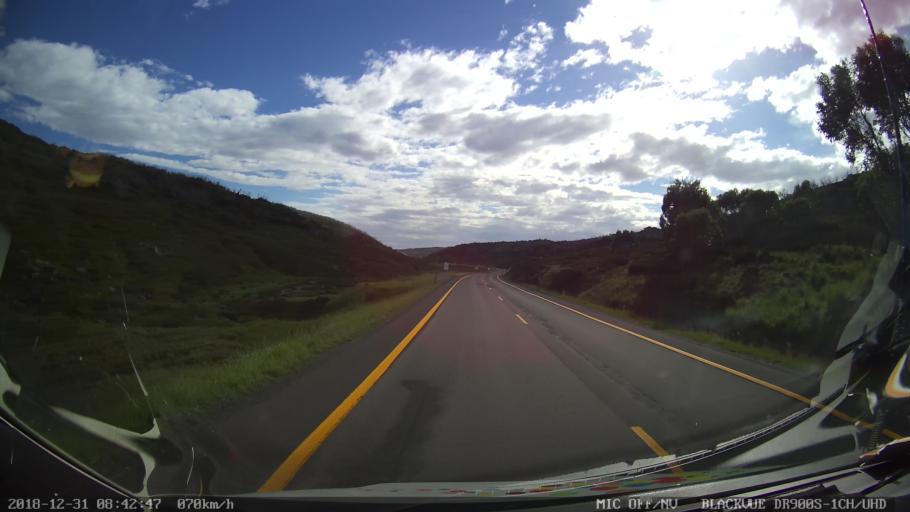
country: AU
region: New South Wales
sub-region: Snowy River
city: Jindabyne
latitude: -36.3924
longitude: 148.4370
